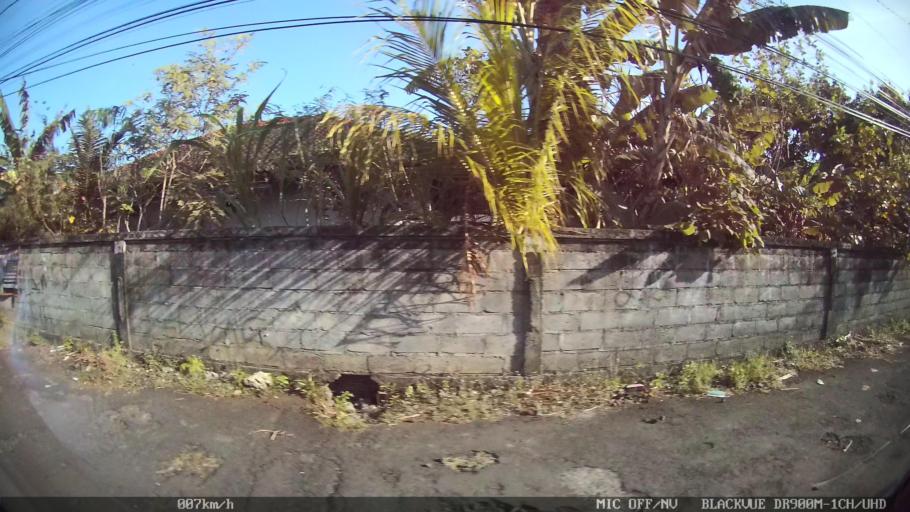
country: ID
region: Bali
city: Jimbaran
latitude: -8.8041
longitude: 115.1838
